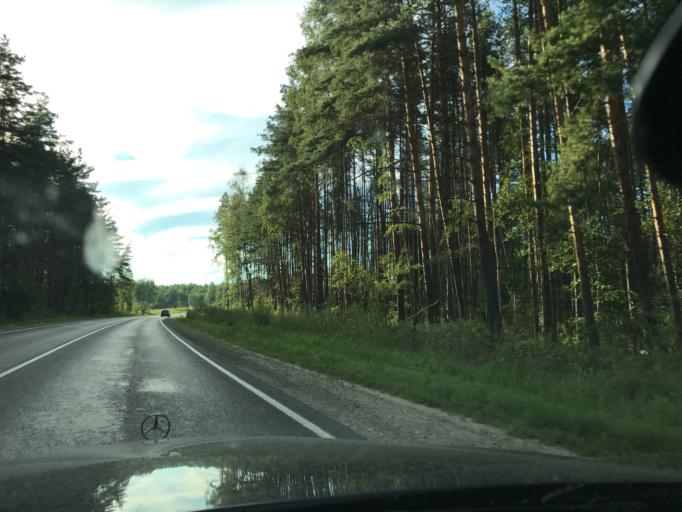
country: RU
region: Vladimir
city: Raduzhnyy
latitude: 56.0318
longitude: 40.3659
